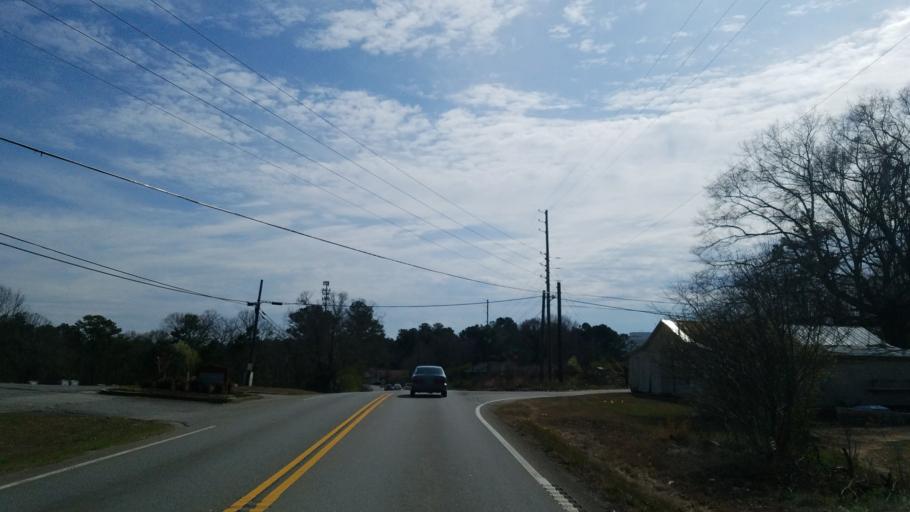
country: US
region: Georgia
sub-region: Cherokee County
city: Canton
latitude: 34.2063
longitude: -84.4553
